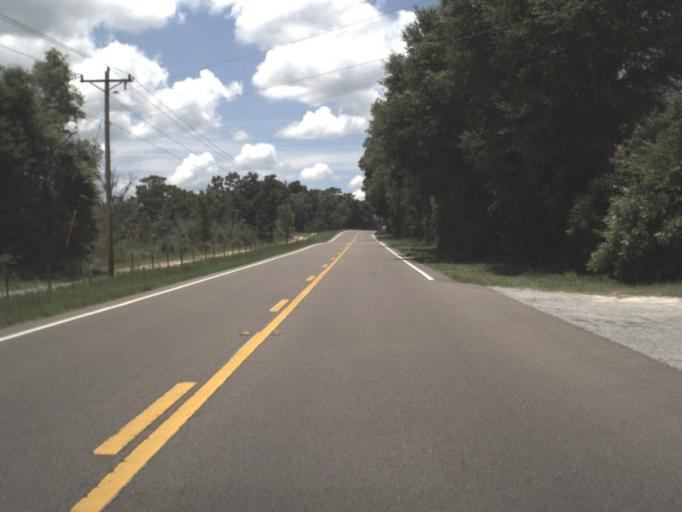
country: US
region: Florida
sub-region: Clay County
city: Keystone Heights
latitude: 29.7309
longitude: -81.9765
